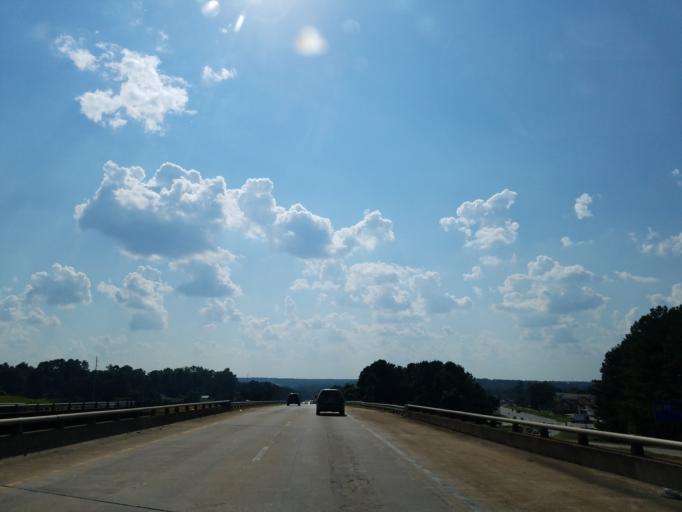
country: US
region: Georgia
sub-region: Clarke County
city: Athens
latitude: 33.9226
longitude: -83.3755
